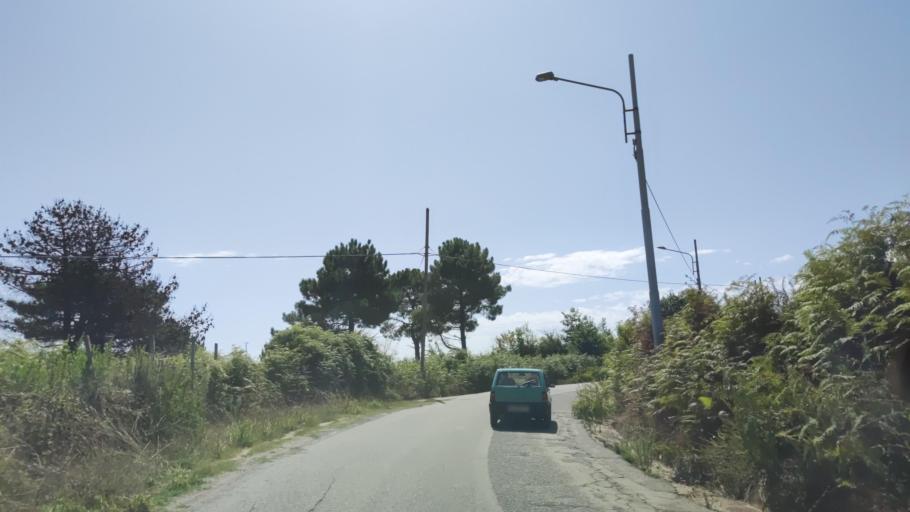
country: IT
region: Calabria
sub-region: Provincia di Reggio Calabria
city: Seminara
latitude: 38.3447
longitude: 15.8432
